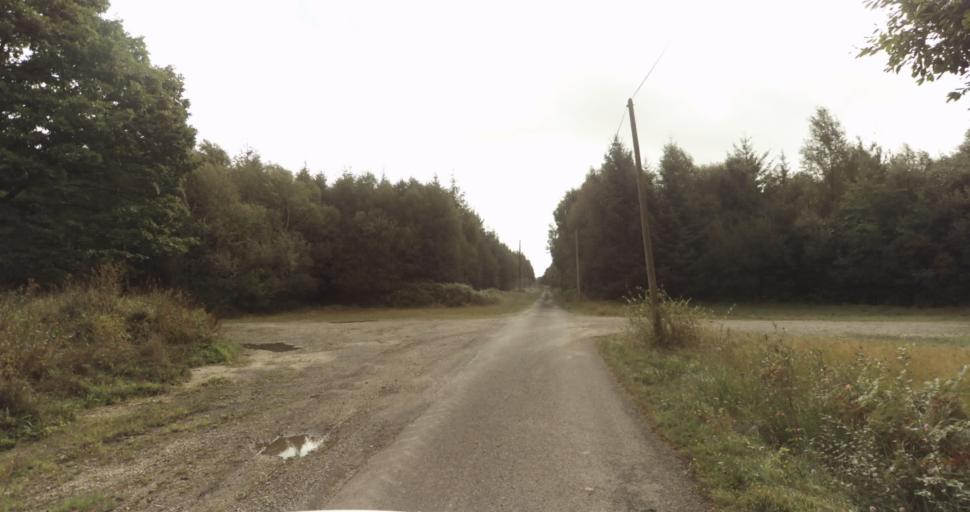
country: FR
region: Lower Normandy
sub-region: Departement de l'Orne
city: Gace
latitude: 48.8385
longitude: 0.3519
